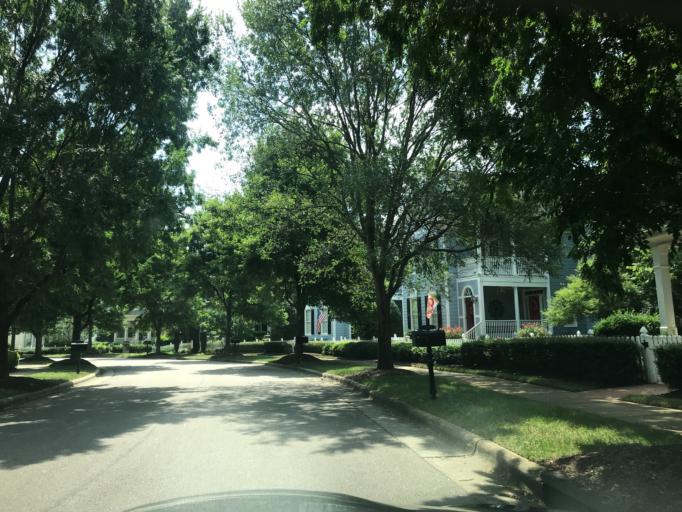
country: US
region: North Carolina
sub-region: Wake County
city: Wake Forest
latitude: 35.9264
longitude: -78.5741
